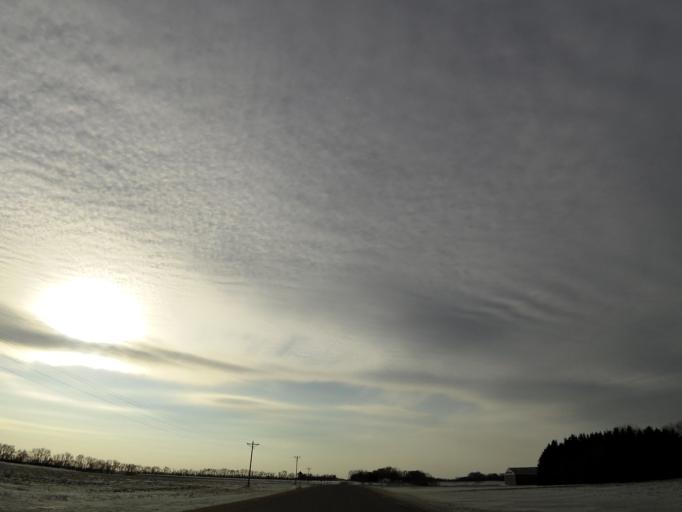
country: US
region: North Dakota
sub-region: Walsh County
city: Grafton
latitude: 48.4267
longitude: -97.3053
